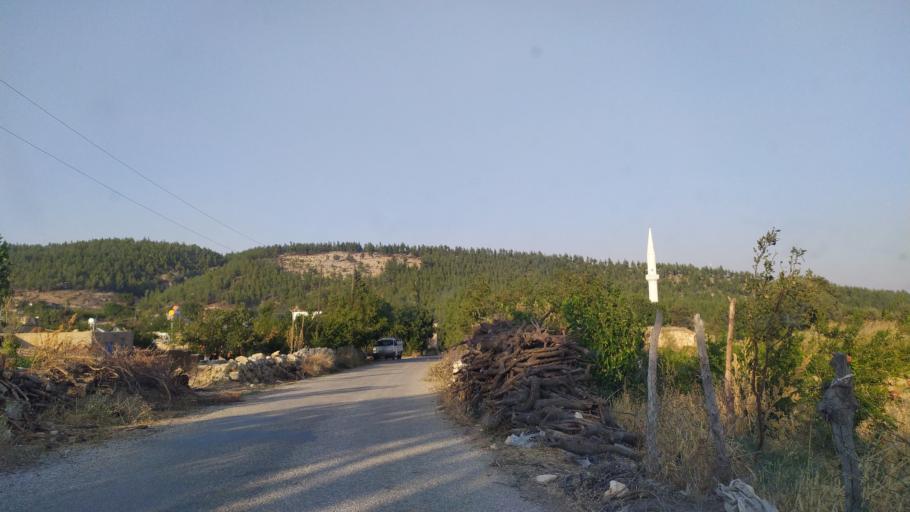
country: TR
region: Mersin
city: Mut
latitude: 36.6920
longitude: 33.1991
